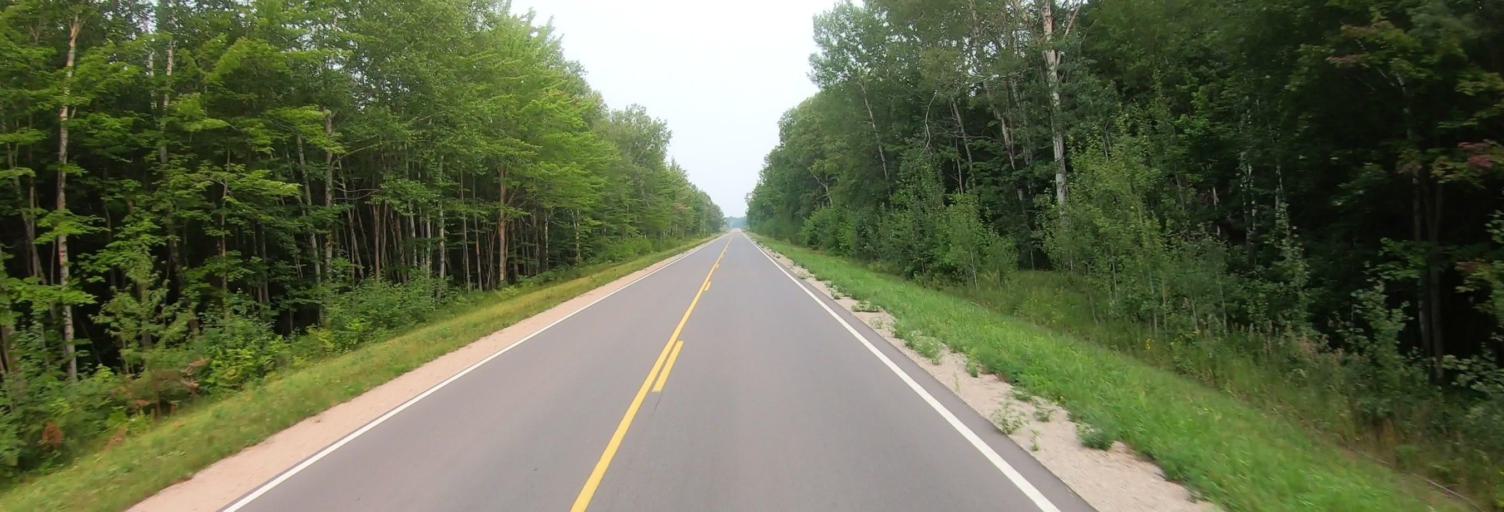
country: US
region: Michigan
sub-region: Luce County
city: Newberry
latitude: 46.4703
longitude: -84.9672
